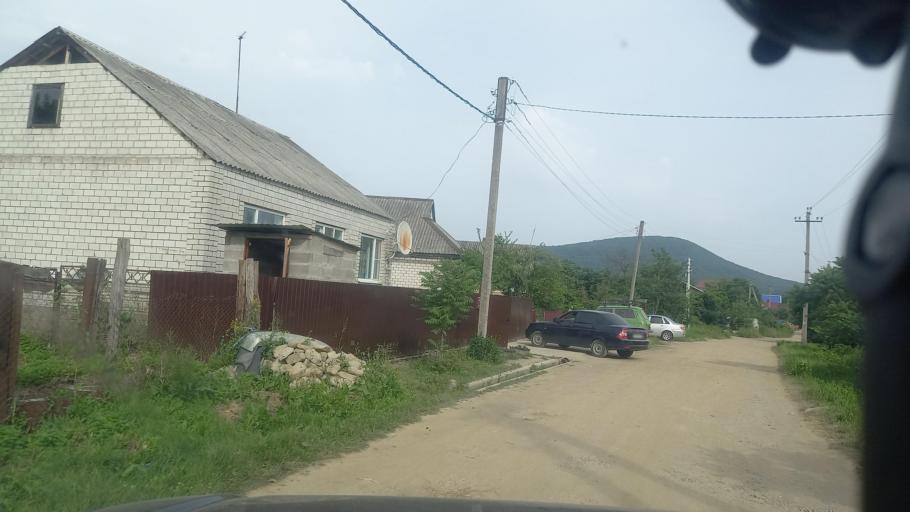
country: RU
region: Krasnodarskiy
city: Goryachiy Klyuch
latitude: 44.6070
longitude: 39.0246
